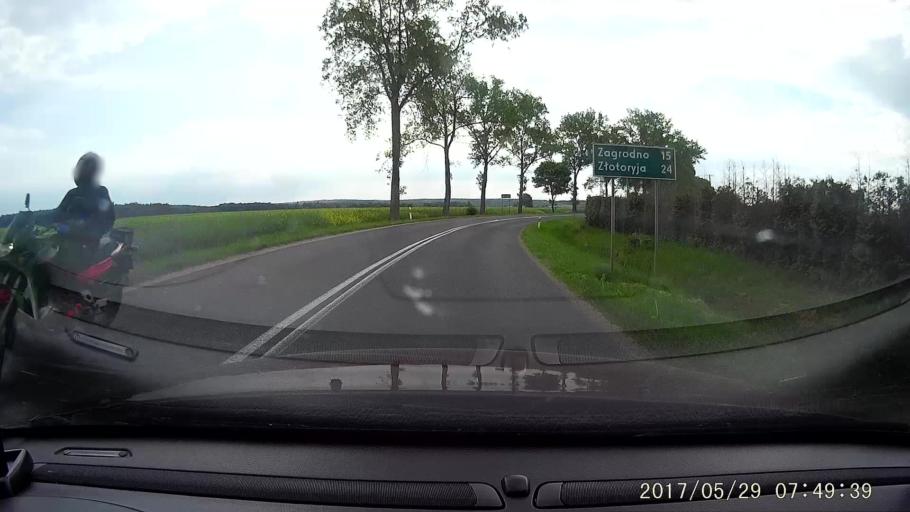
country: PL
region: Lower Silesian Voivodeship
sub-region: Powiat boleslawiecki
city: Boleslawiec
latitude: 51.2273
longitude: 15.6817
